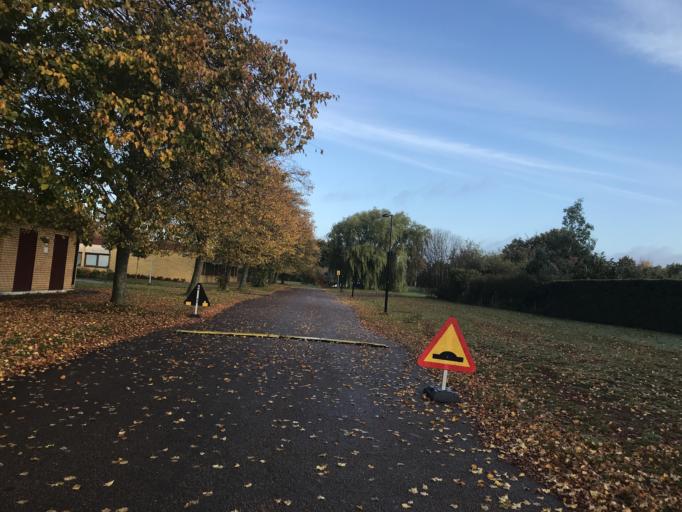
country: SE
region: Skane
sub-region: Landskrona
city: Landskrona
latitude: 55.8870
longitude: 12.8197
